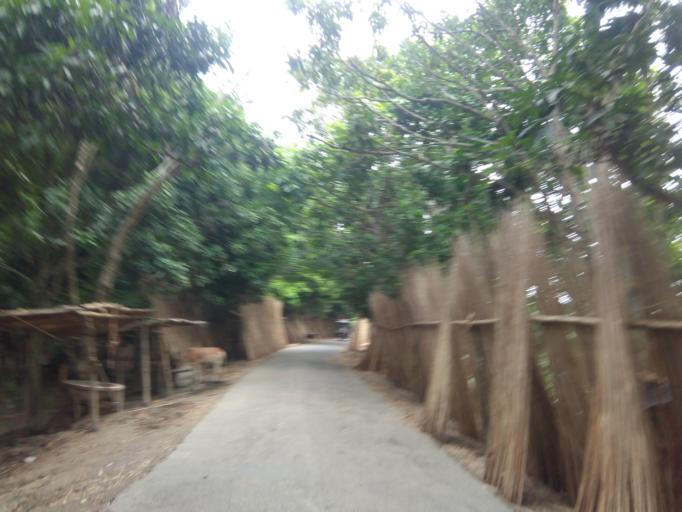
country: BD
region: Khulna
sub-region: Magura
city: Magura
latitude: 23.4473
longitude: 89.6278
